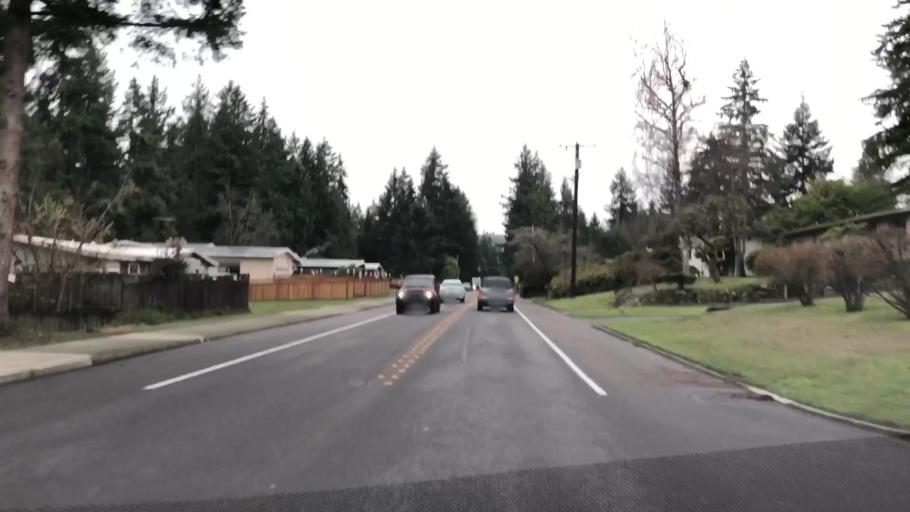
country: US
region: Washington
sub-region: King County
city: Eastgate
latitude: 47.5879
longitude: -122.1324
